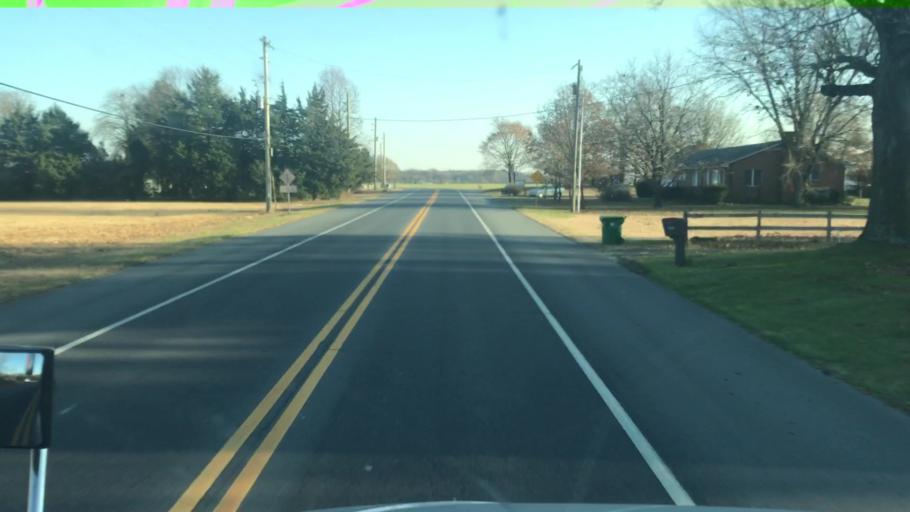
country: US
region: Delaware
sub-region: Sussex County
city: Bridgeville
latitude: 38.7915
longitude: -75.6899
